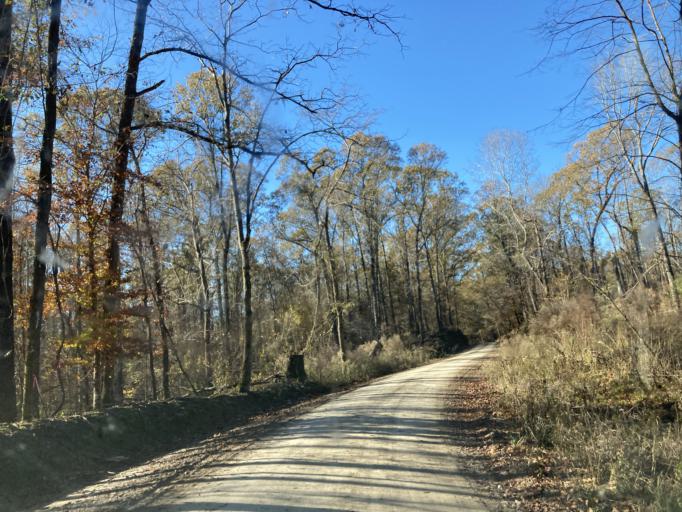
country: US
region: Mississippi
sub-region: Yazoo County
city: Yazoo City
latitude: 32.6740
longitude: -90.5062
